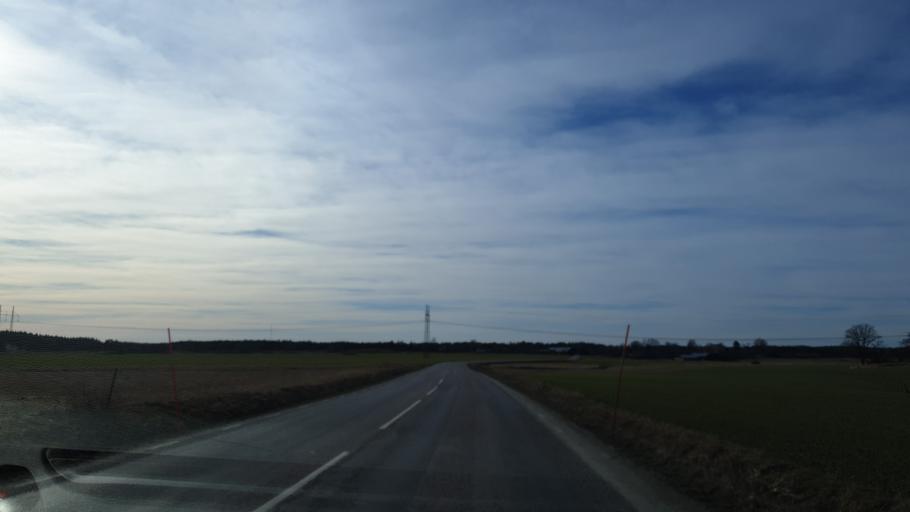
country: SE
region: Uppsala
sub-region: Enkopings Kommun
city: Grillby
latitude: 59.5927
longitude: 17.1954
